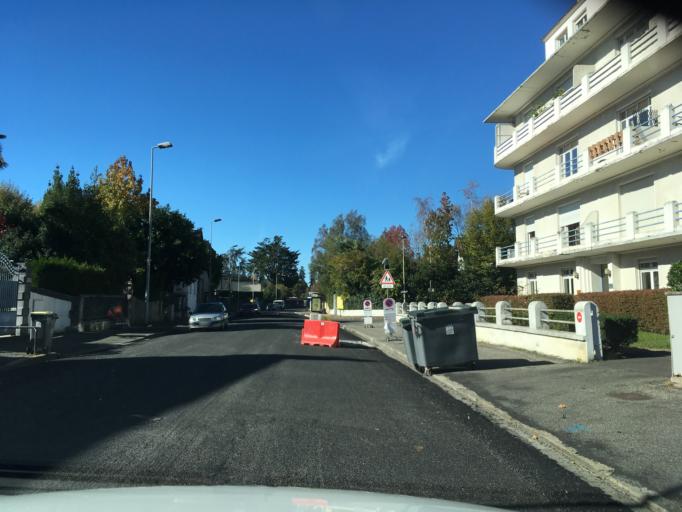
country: FR
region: Aquitaine
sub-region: Departement des Pyrenees-Atlantiques
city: Bizanos
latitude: 43.2990
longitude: -0.3488
